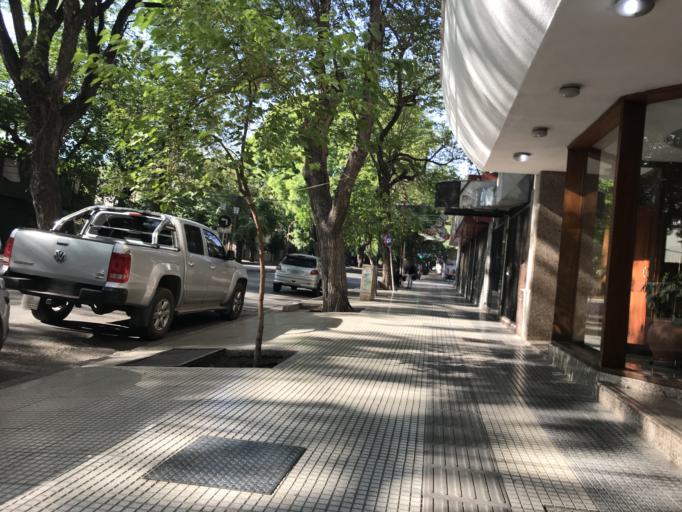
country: AR
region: Mendoza
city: Mendoza
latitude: -32.8836
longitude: -68.8430
